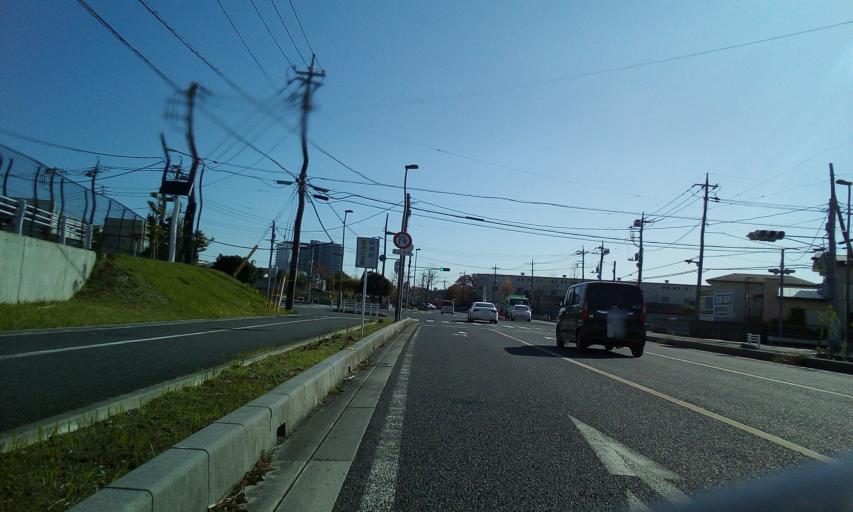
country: JP
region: Saitama
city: Yoshikawa
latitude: 35.8619
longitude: 139.8617
